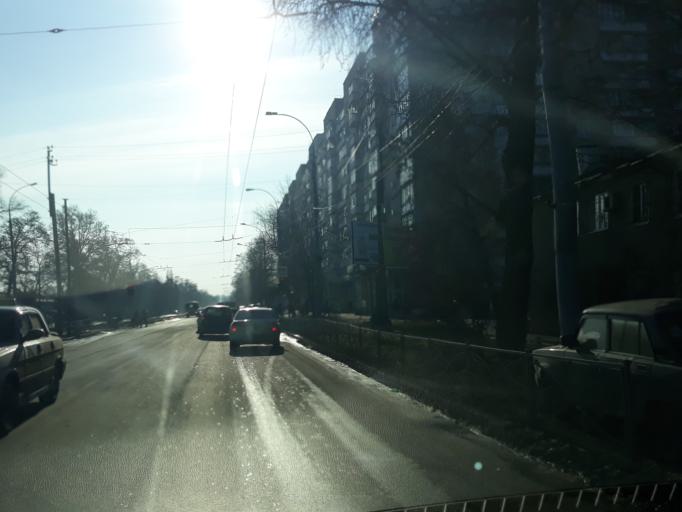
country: RU
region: Rostov
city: Taganrog
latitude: 47.2292
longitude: 38.9076
